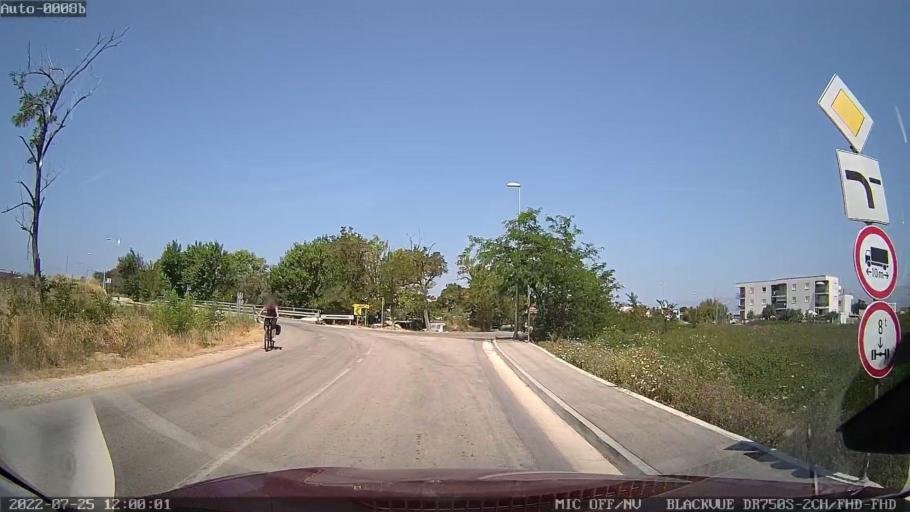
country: HR
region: Zadarska
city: Nin
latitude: 44.2431
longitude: 15.1965
